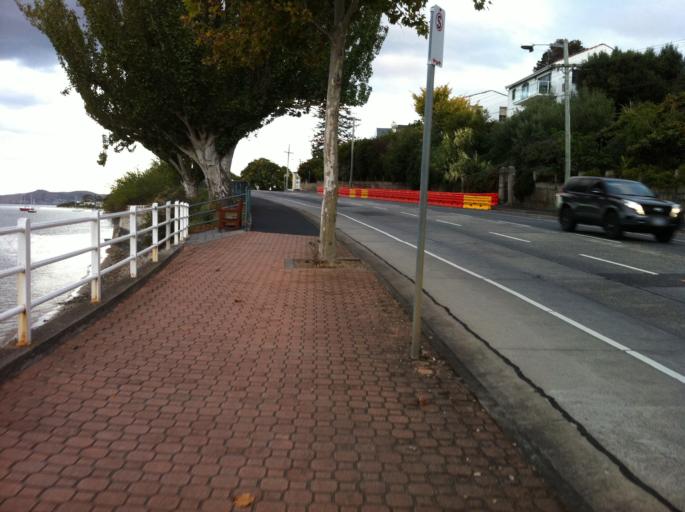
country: AU
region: Tasmania
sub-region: Hobart
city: Sandy Bay
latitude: -42.9055
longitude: 147.3397
